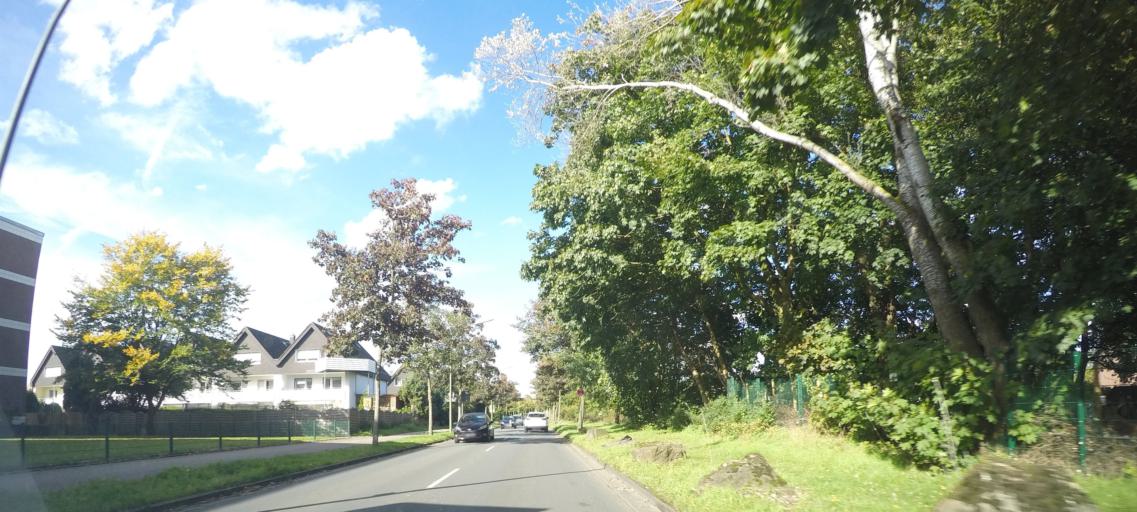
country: DE
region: North Rhine-Westphalia
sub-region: Regierungsbezirk Arnsberg
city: Hamm
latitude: 51.6907
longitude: 7.8826
